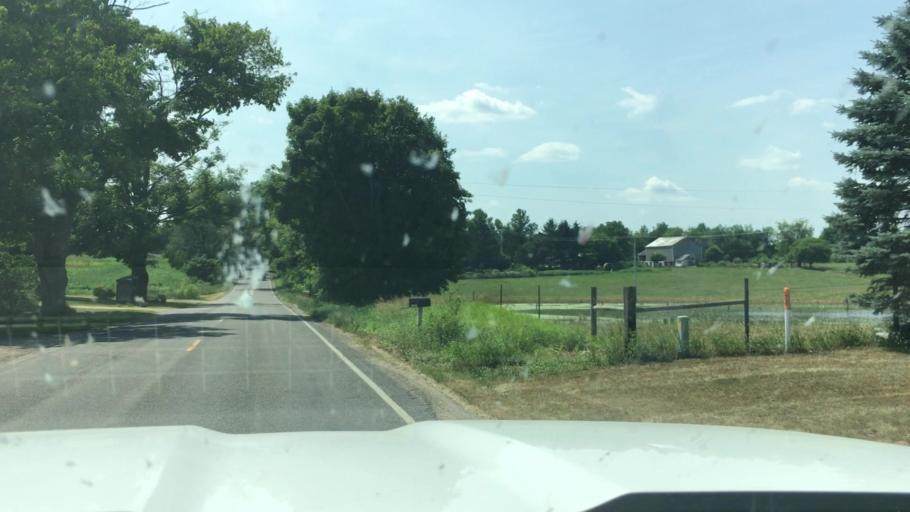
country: US
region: Michigan
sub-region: Barry County
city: Stony Point
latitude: 42.4285
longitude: -85.4927
